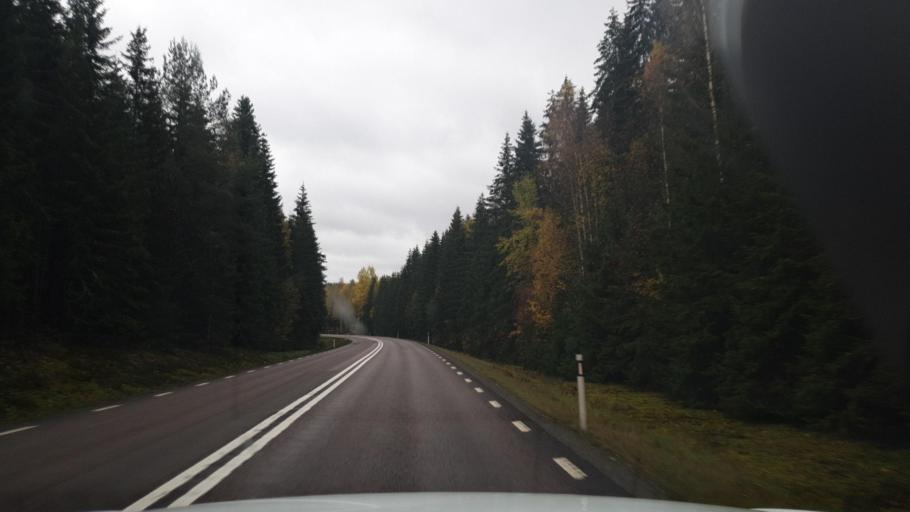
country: SE
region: Vaermland
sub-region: Arvika Kommun
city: Arvika
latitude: 59.7186
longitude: 12.5255
